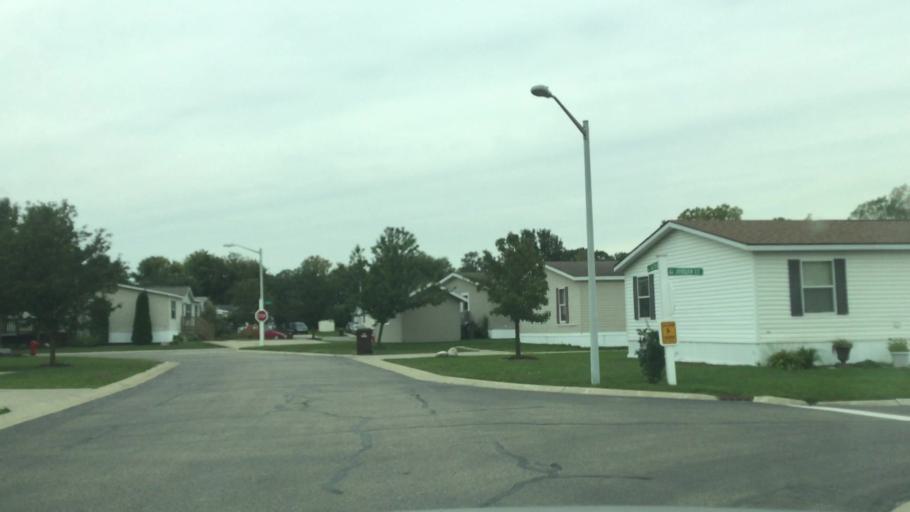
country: US
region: Michigan
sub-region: Oakland County
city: Waterford
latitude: 42.6609
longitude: -83.4716
